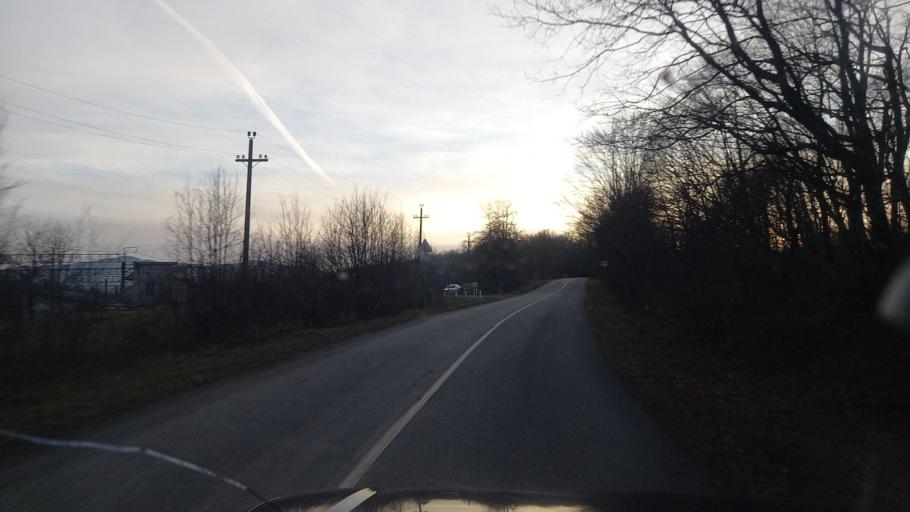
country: RU
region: Krasnodarskiy
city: Goryachiy Klyuch
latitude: 44.3892
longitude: 39.1916
